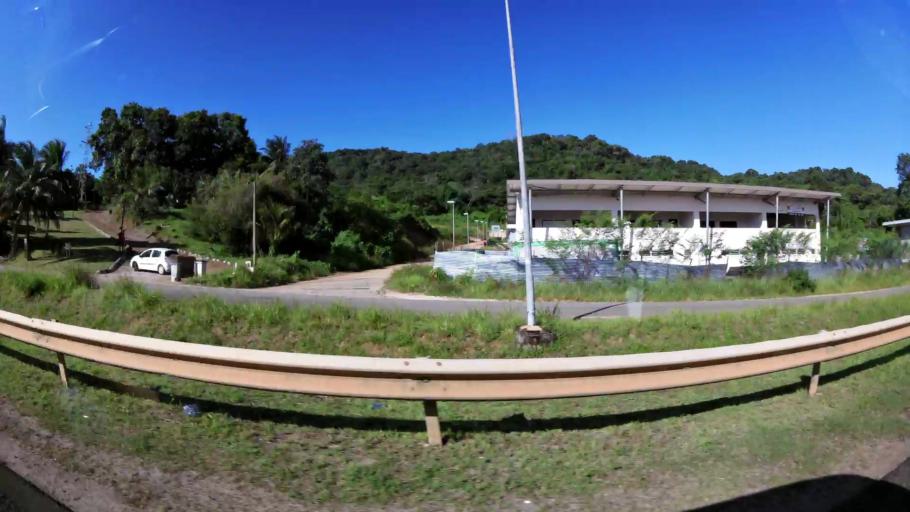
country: GF
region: Guyane
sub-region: Guyane
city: Remire-Montjoly
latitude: 4.8700
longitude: -52.2760
